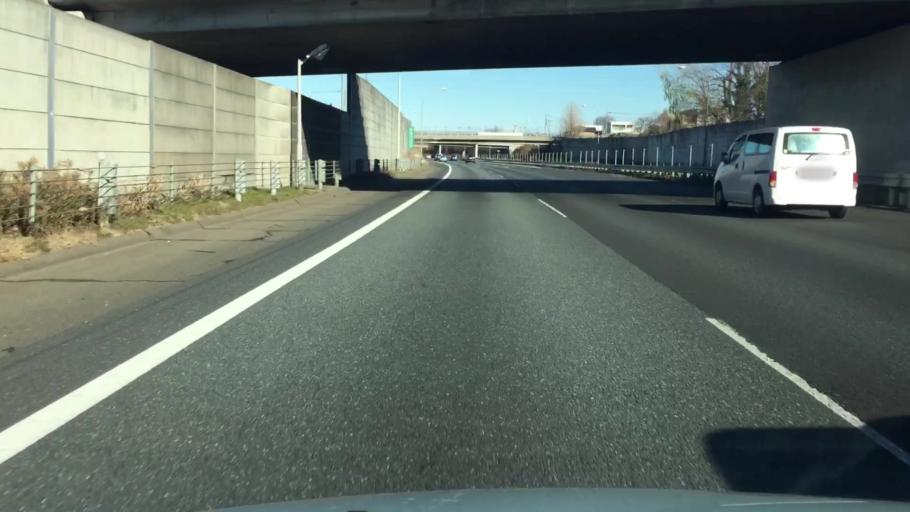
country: JP
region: Saitama
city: Sakado
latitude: 35.9994
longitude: 139.3879
